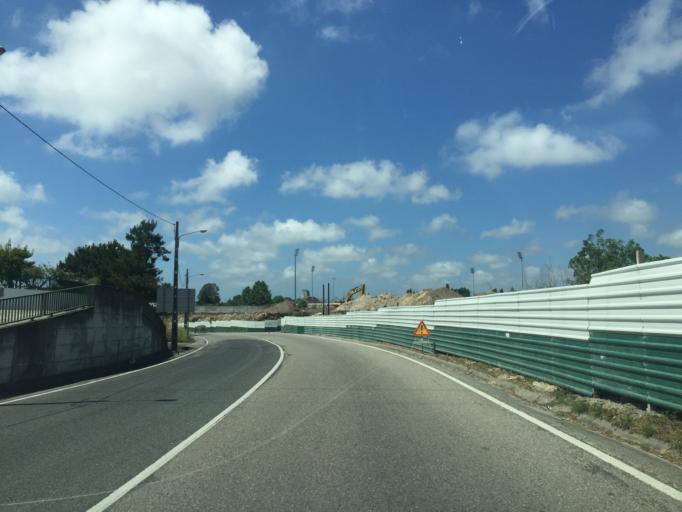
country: PT
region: Leiria
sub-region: Marinha Grande
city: Marinha Grande
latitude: 39.7328
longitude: -8.9299
